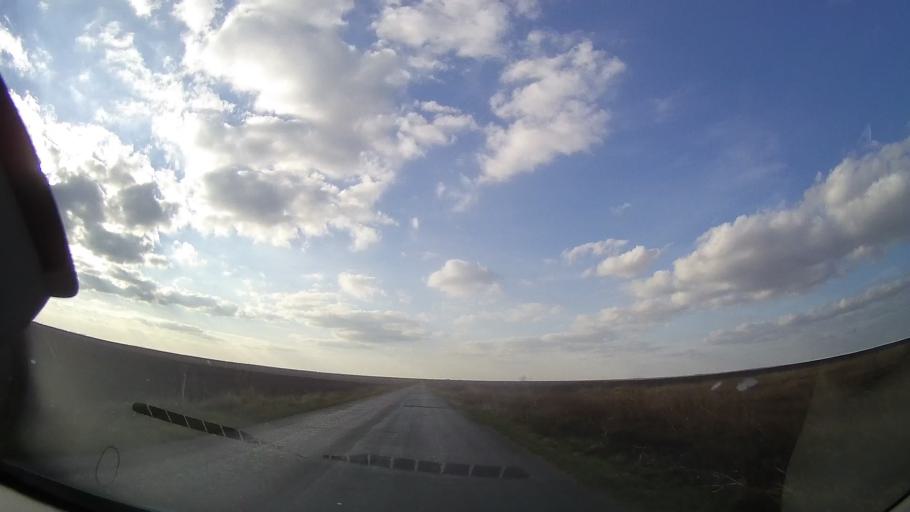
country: RO
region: Constanta
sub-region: Comuna Negru Voda
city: Negru Voda
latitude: 43.8202
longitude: 28.1743
